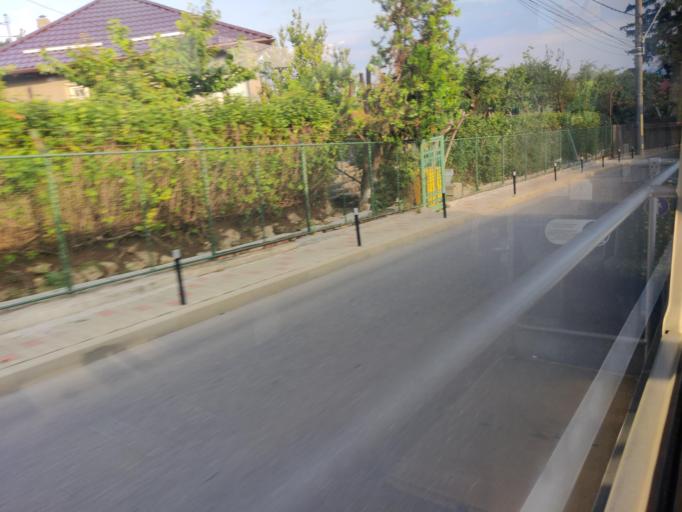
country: RO
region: Iasi
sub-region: Municipiul Iasi
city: Iasi
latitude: 47.1701
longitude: 27.5998
